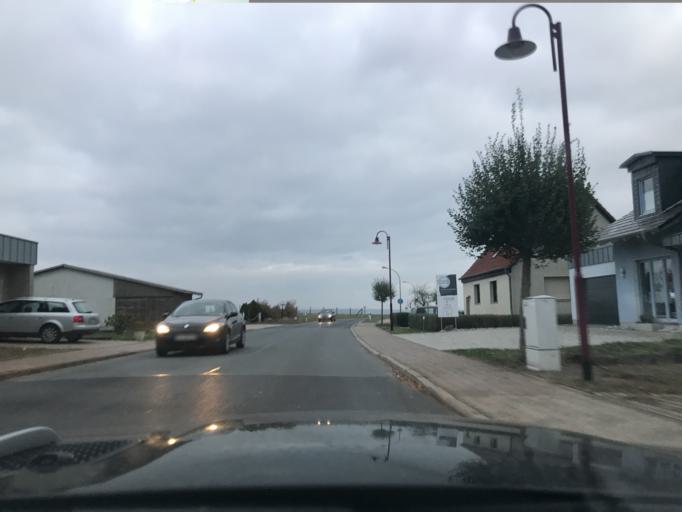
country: DE
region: Thuringia
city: Kullstedt
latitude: 51.2773
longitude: 10.2837
